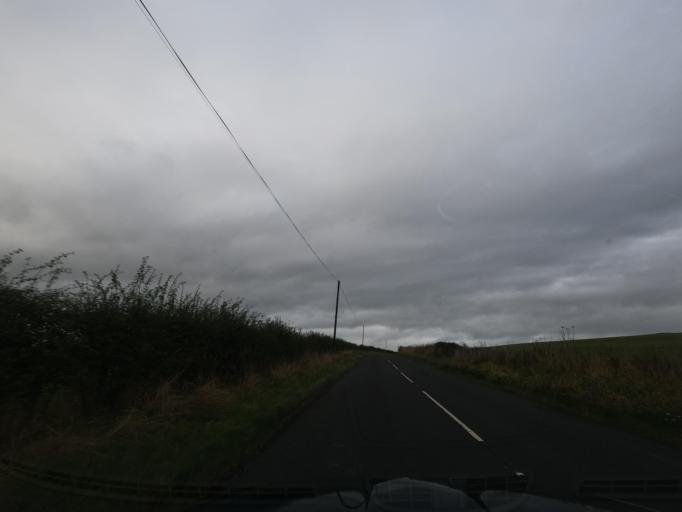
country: GB
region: England
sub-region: Northumberland
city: Doddington
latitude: 55.5939
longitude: -2.0028
